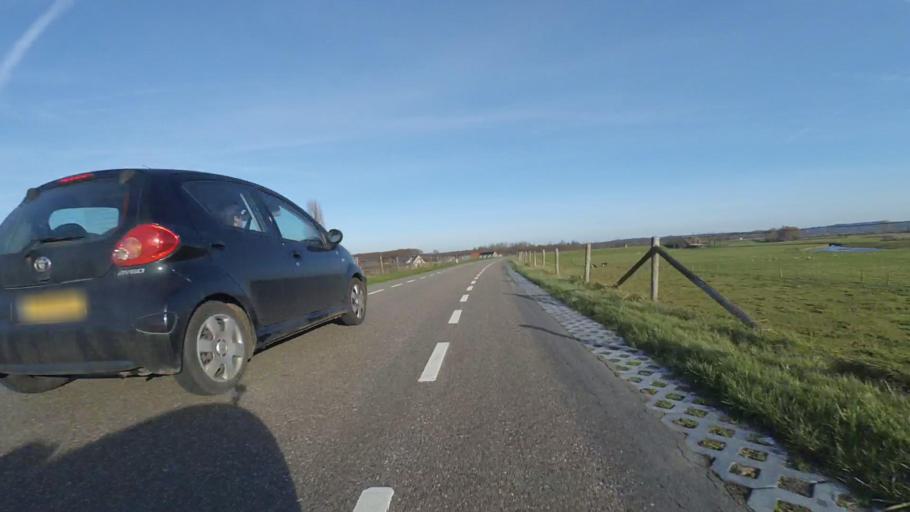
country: NL
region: Utrecht
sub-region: Gemeente Utrechtse Heuvelrug
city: Leersum
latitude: 51.9858
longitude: 5.4228
